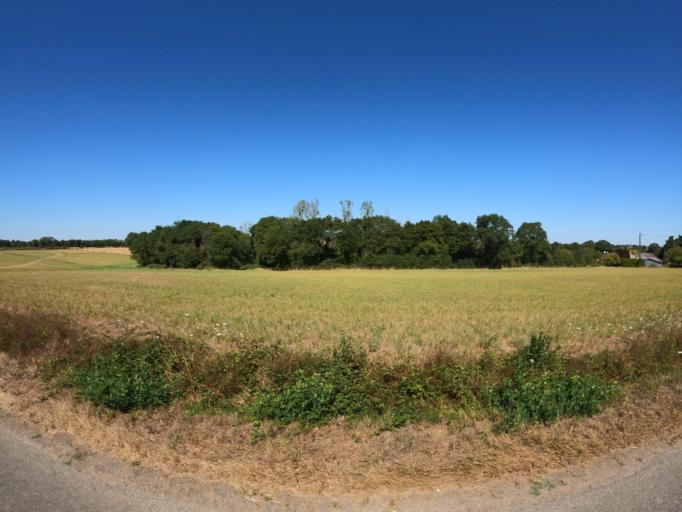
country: FR
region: Pays de la Loire
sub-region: Departement de Maine-et-Loire
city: Saint-Christophe-du-Bois
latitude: 47.0471
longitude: -0.9590
